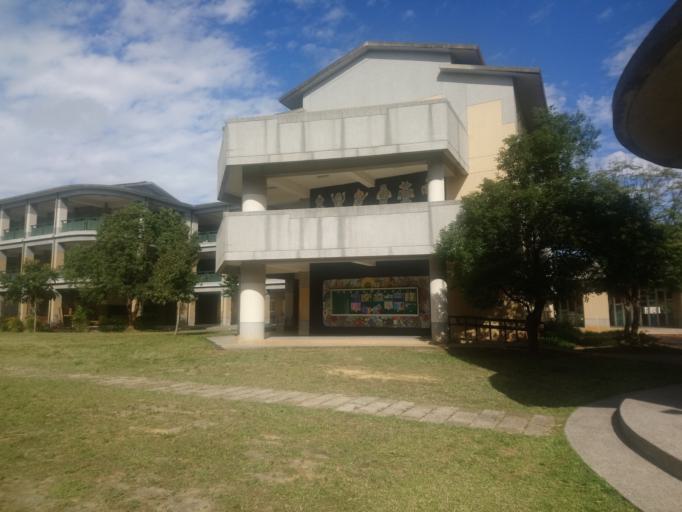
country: TW
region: Taiwan
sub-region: Hsinchu
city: Hsinchu
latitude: 24.7800
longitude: 120.9836
